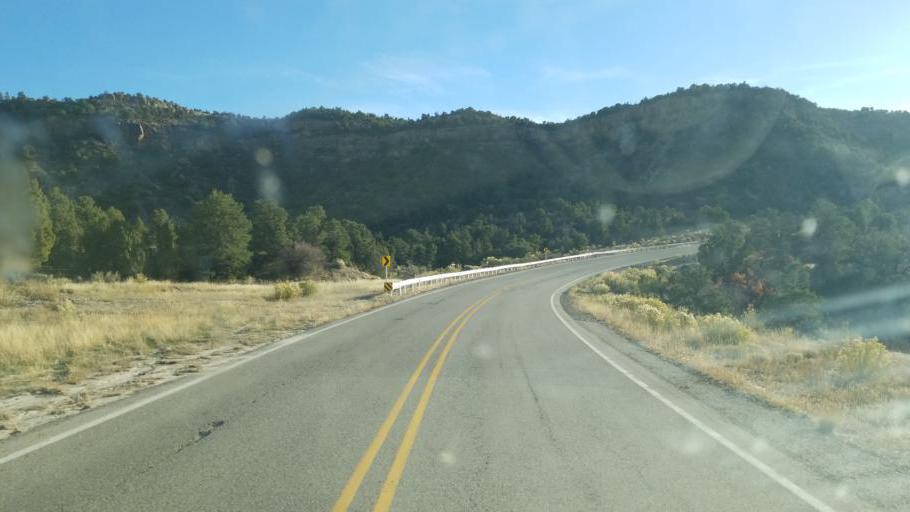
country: US
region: New Mexico
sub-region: San Juan County
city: Bloomfield
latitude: 36.7265
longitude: -107.6560
